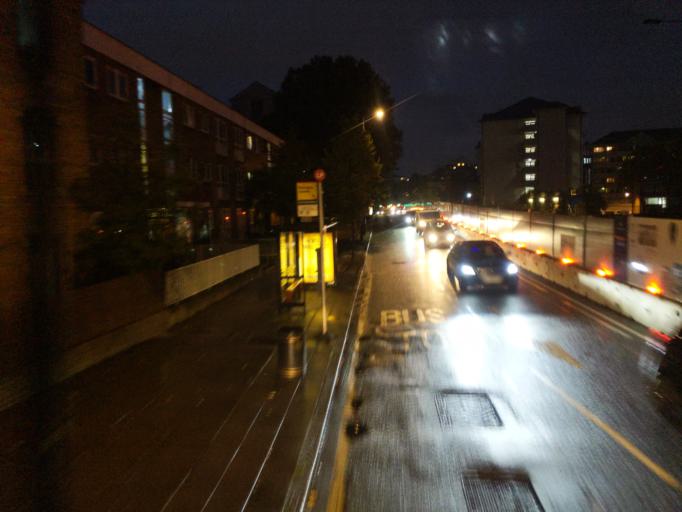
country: GB
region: England
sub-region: Greater London
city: Bayswater
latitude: 51.5249
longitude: -0.1687
